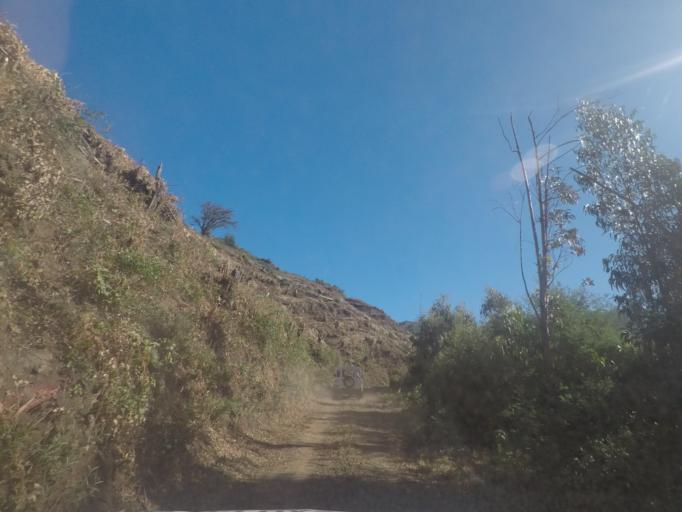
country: PT
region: Madeira
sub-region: Funchal
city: Nossa Senhora do Monte
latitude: 32.6935
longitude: -16.9112
